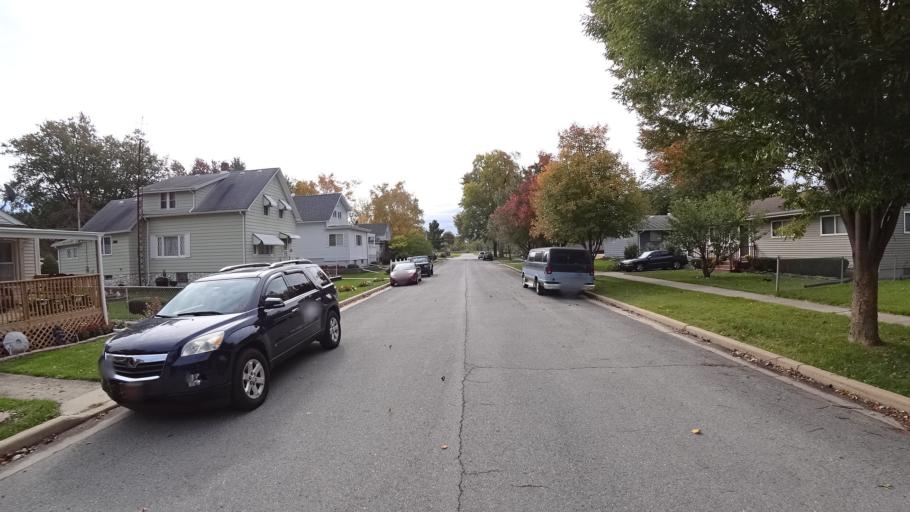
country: US
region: Indiana
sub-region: LaPorte County
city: Michigan City
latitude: 41.7024
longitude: -86.8996
